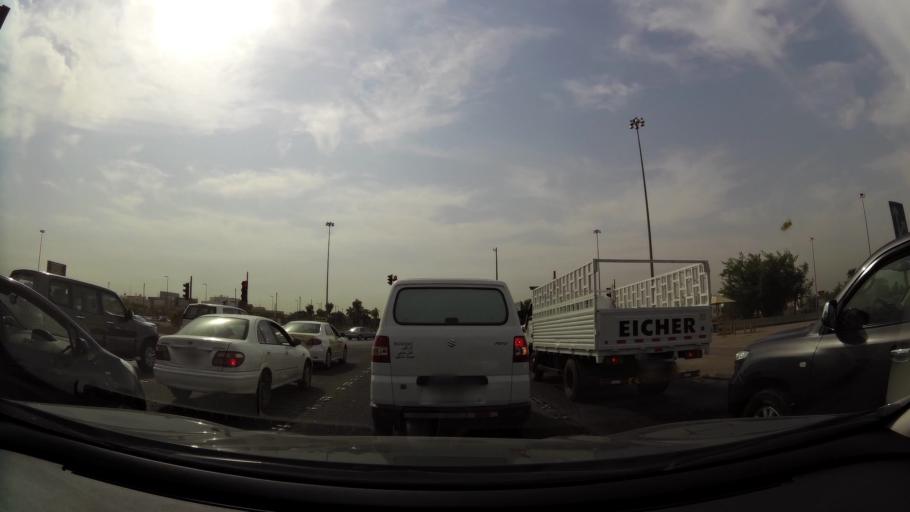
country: KW
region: Al Asimah
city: Kuwait City
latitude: 29.3596
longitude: 47.9737
